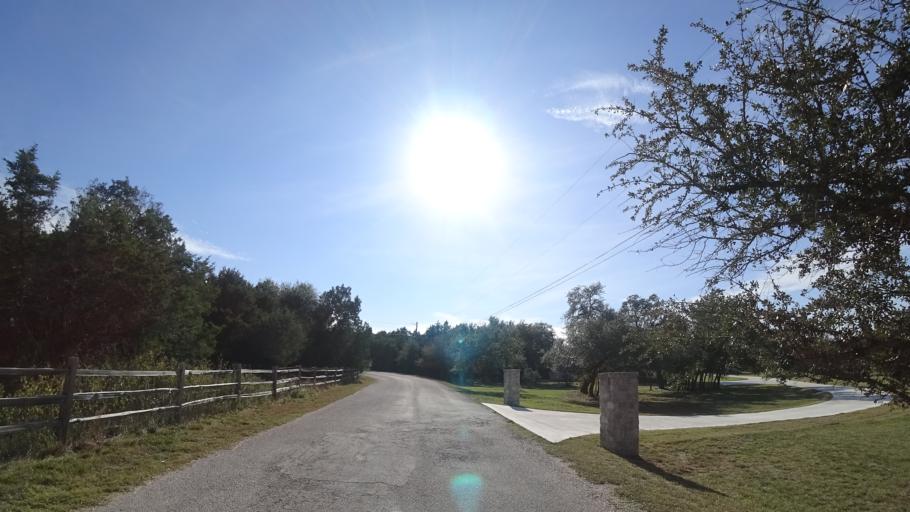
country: US
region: Texas
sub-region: Travis County
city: Bee Cave
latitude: 30.2356
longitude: -97.9412
